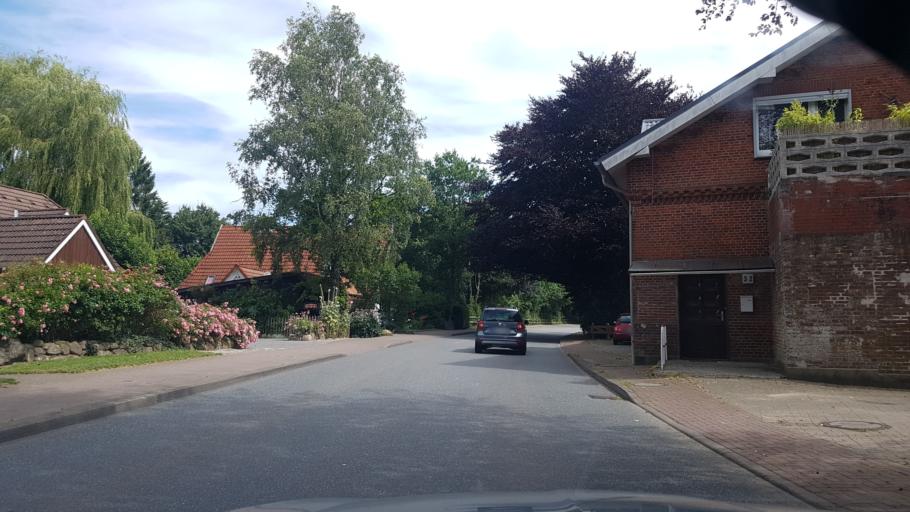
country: DE
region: Schleswig-Holstein
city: Gross Buchwald
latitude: 54.1626
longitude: 10.0856
